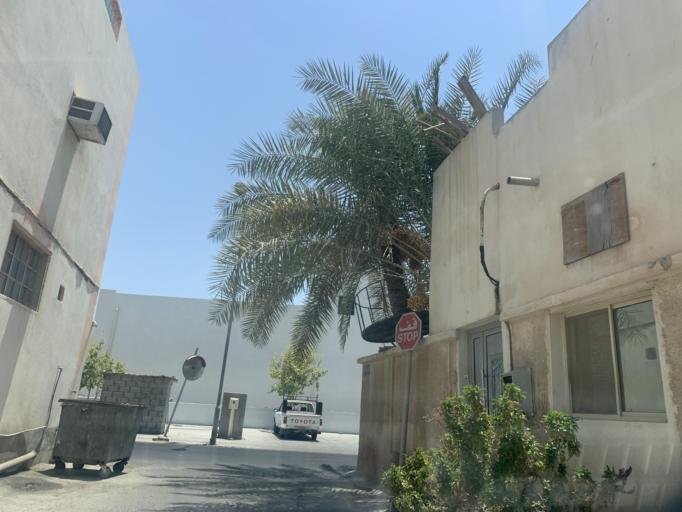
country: BH
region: Muharraq
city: Al Muharraq
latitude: 26.2828
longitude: 50.6208
